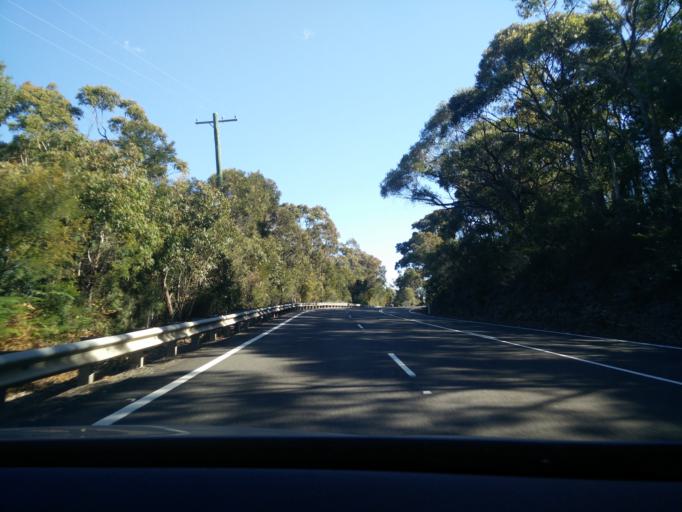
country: AU
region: New South Wales
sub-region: Hornsby Shire
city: Berowra
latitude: -33.5778
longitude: 151.1864
